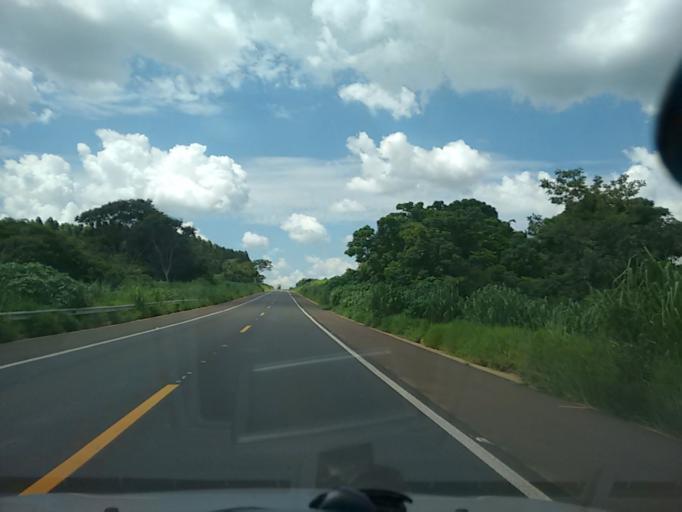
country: BR
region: Sao Paulo
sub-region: Osvaldo Cruz
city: Osvaldo Cruz
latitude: -21.8395
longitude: -50.8268
